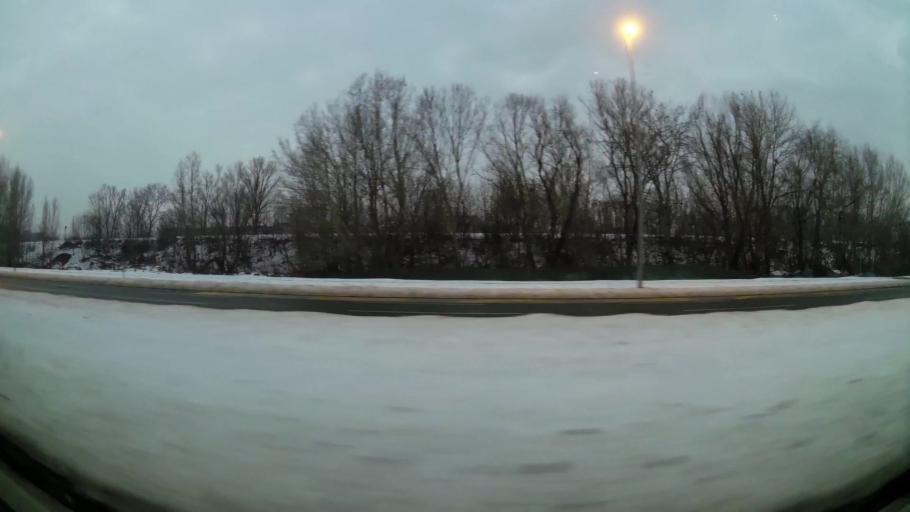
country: RS
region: Central Serbia
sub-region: Belgrade
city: Novi Beograd
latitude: 44.8151
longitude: 20.3979
